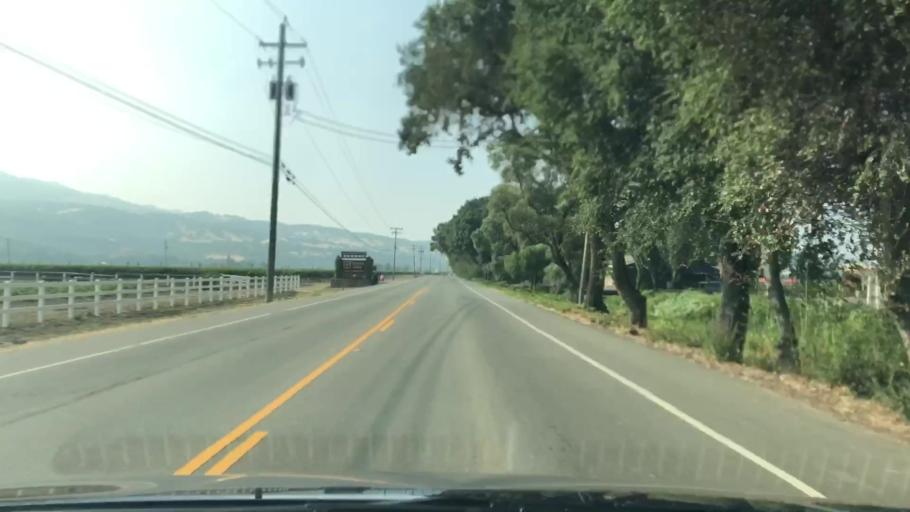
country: US
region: California
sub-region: Solano County
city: Green Valley
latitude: 38.2759
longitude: -122.1129
